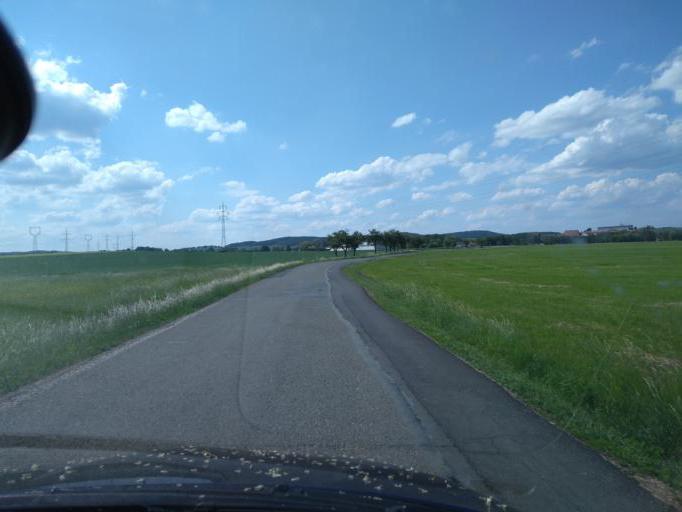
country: CZ
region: Plzensky
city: Merklin
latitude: 49.5922
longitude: 13.2534
